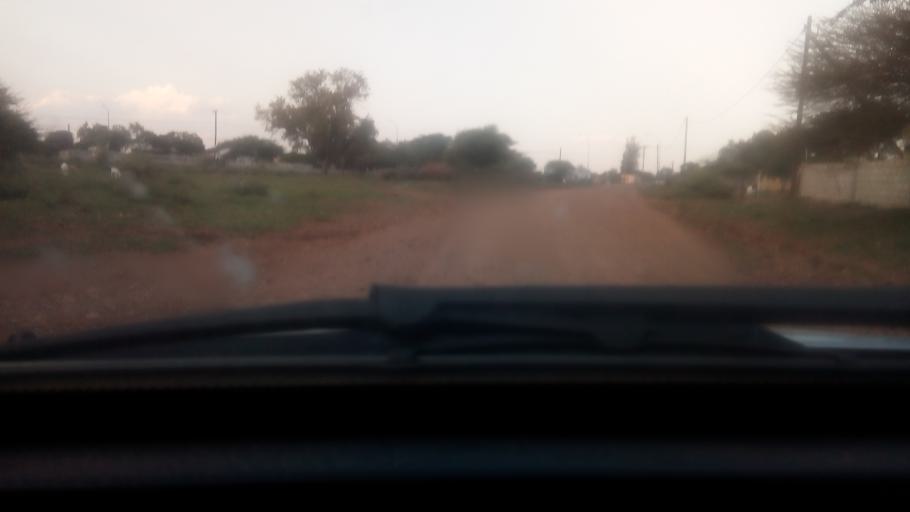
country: BW
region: Kgatleng
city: Bokaa
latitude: -24.4275
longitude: 26.0156
